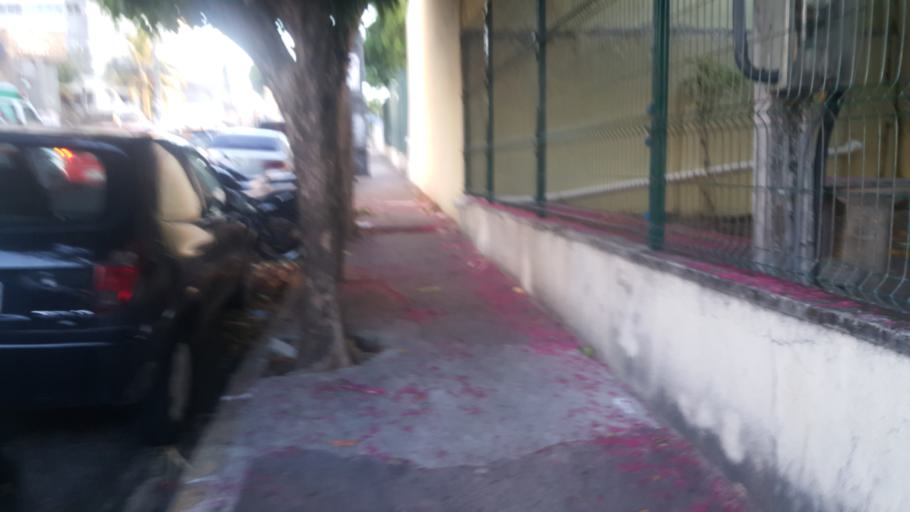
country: BR
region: Ceara
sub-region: Fortaleza
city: Fortaleza
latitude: -3.7405
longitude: -38.5109
